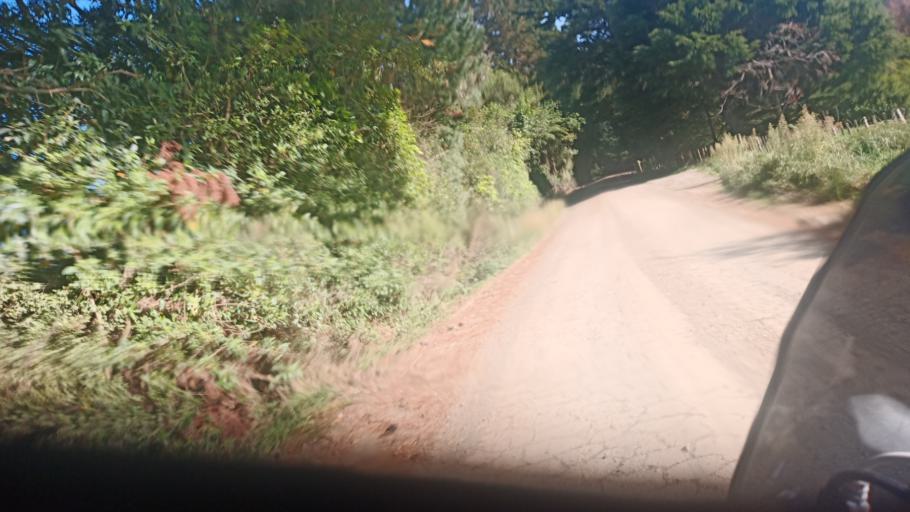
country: NZ
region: Bay of Plenty
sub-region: Opotiki District
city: Opotiki
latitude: -38.4350
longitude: 177.5501
